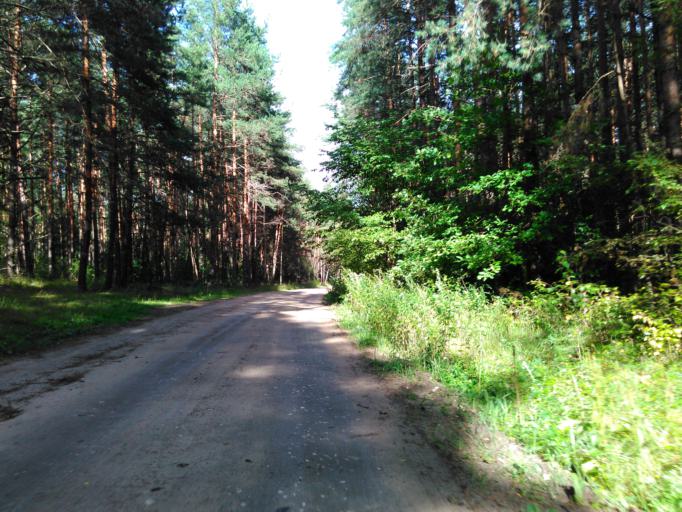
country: RU
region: Vladimir
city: Pokrov
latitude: 55.9716
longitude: 39.0862
